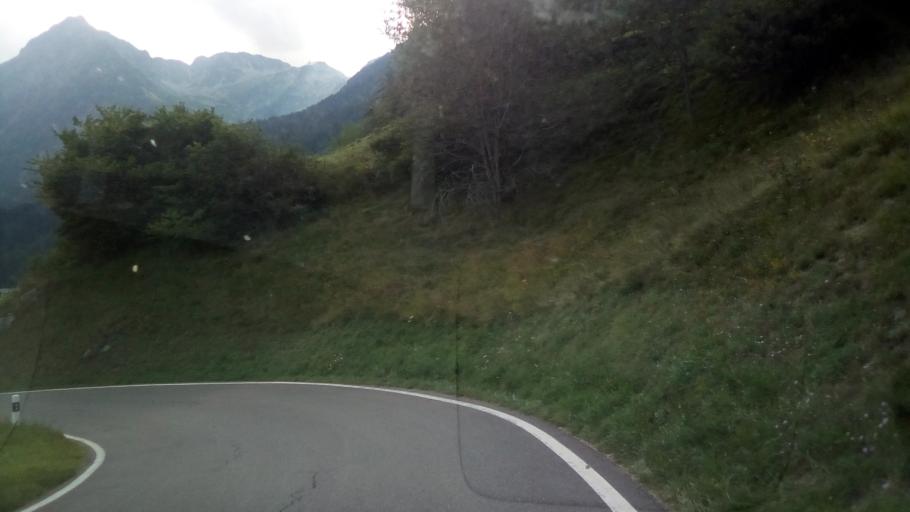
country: CH
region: Valais
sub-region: Entremont District
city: Orsieres
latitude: 46.0252
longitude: 7.1322
